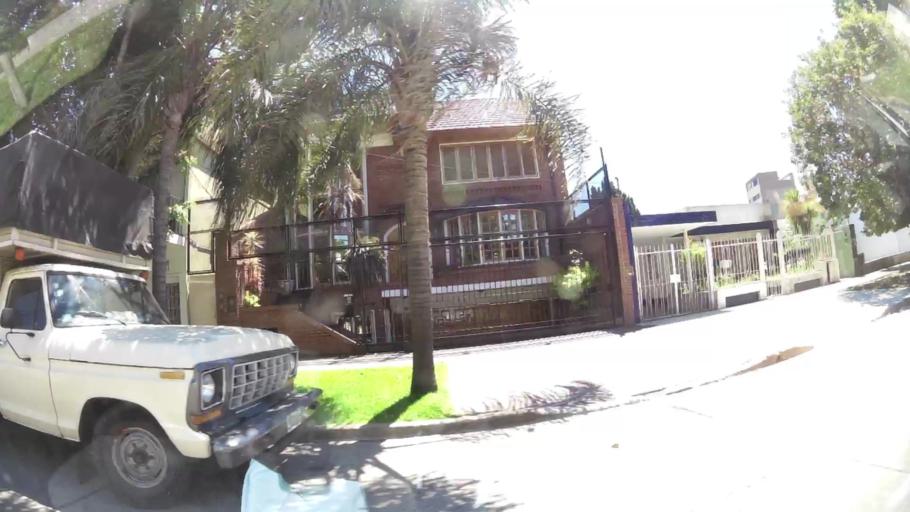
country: AR
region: Buenos Aires
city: Caseros
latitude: -34.5857
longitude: -58.5702
